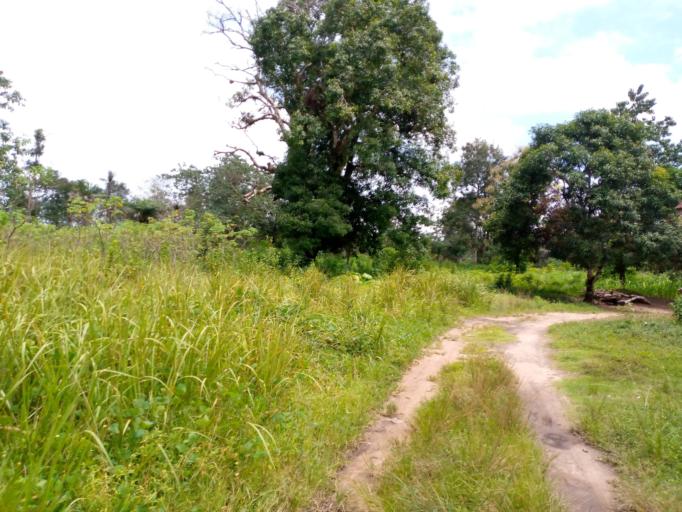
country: SL
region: Northern Province
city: Magburaka
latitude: 8.7248
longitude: -11.9300
